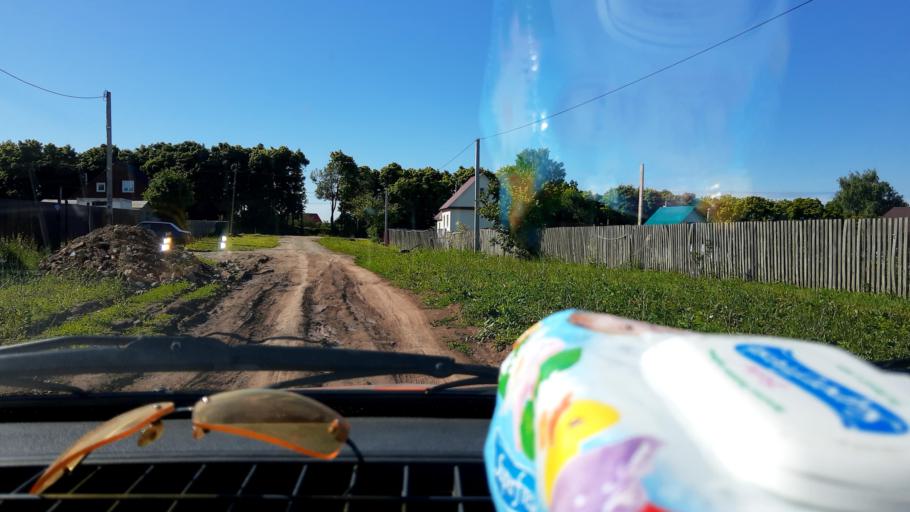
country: RU
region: Bashkortostan
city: Blagoveshchensk
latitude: 55.0640
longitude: 55.9368
